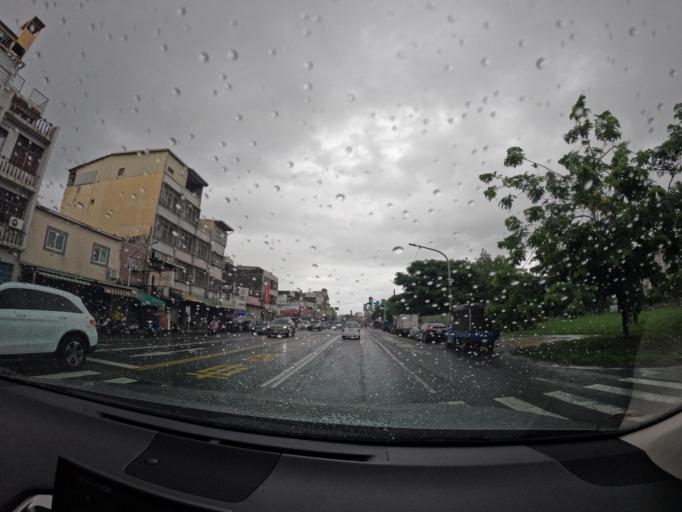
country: TW
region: Taiwan
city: Fengshan
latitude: 22.6443
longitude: 120.3648
